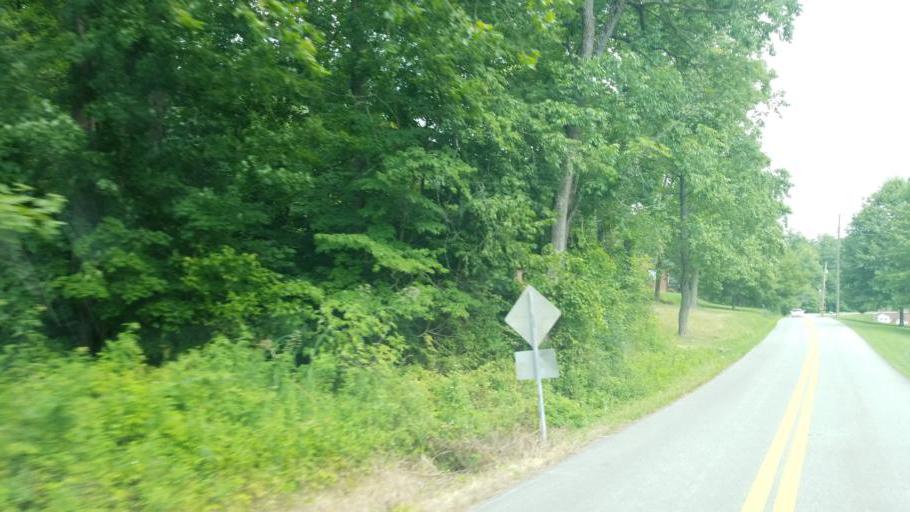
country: US
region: West Virginia
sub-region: Kanawha County
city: Alum Creek
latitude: 38.3144
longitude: -81.7947
